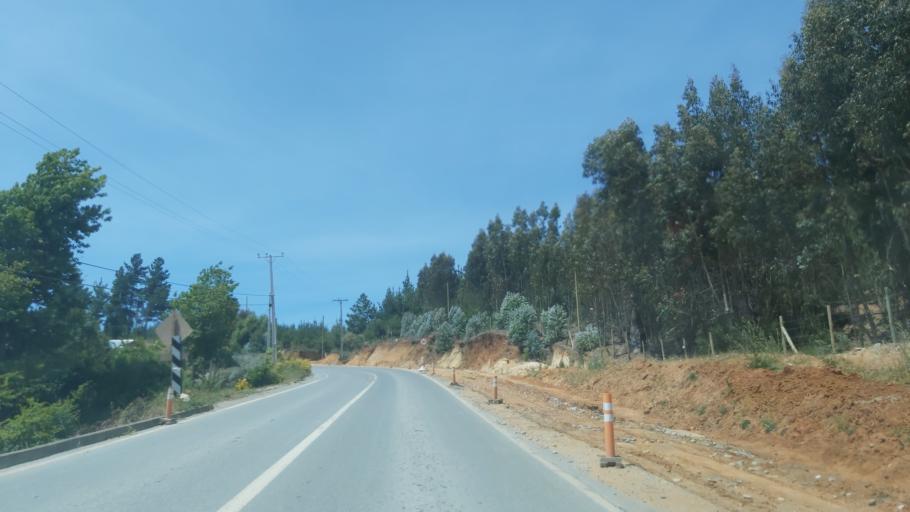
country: CL
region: Maule
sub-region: Provincia de Talca
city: Constitucion
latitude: -35.4430
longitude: -72.4597
